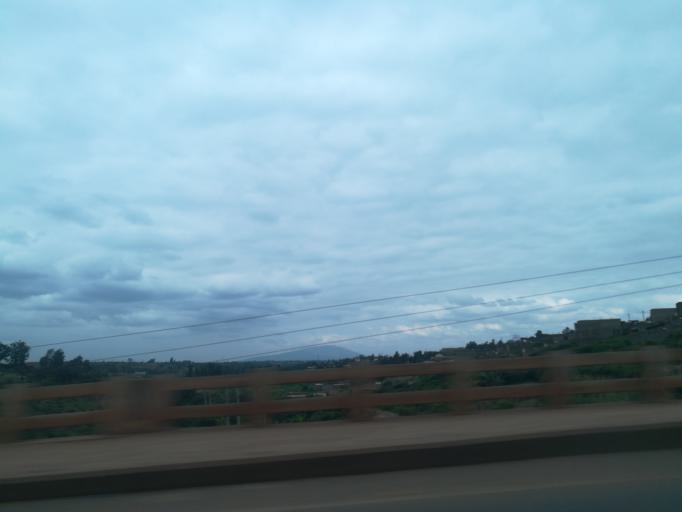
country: KE
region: Nairobi Area
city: Thika
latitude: -1.0630
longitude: 37.0536
